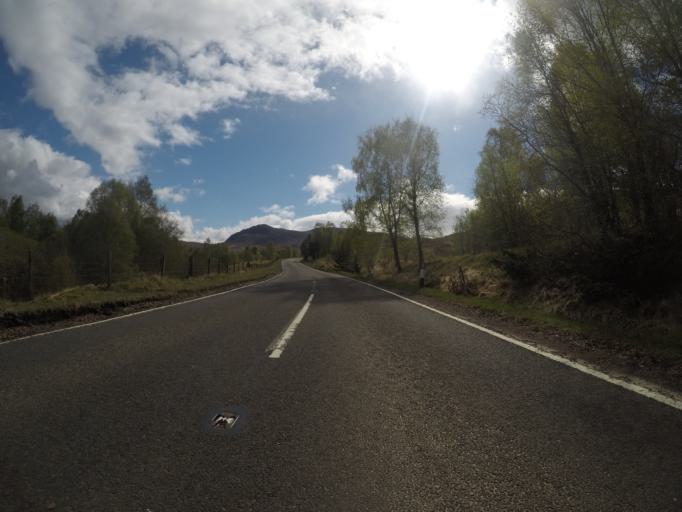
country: GB
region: Scotland
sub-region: Highland
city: Spean Bridge
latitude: 57.1426
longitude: -4.9562
